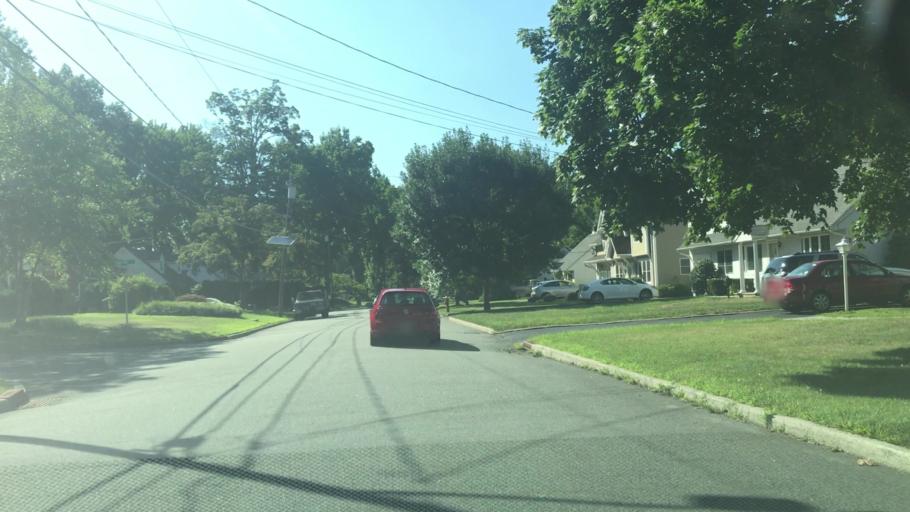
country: US
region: New Jersey
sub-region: Bergen County
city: Maywood
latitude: 40.9186
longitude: -74.0556
